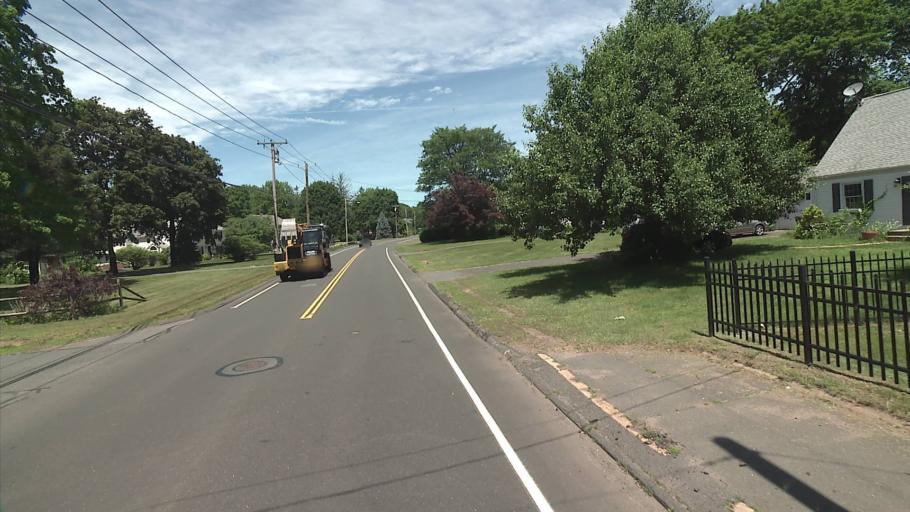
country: US
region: Connecticut
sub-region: New Haven County
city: Meriden
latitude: 41.5889
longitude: -72.8736
